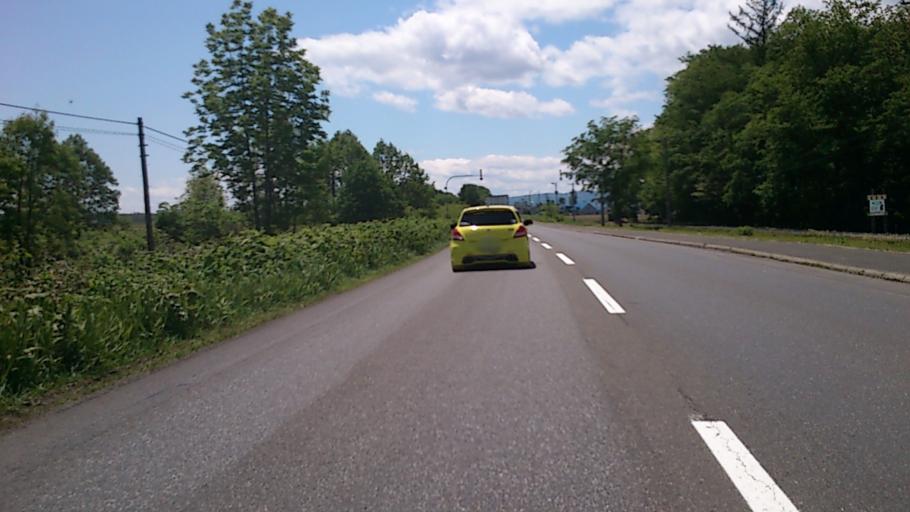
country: JP
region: Hokkaido
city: Nayoro
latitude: 44.3046
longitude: 142.4352
